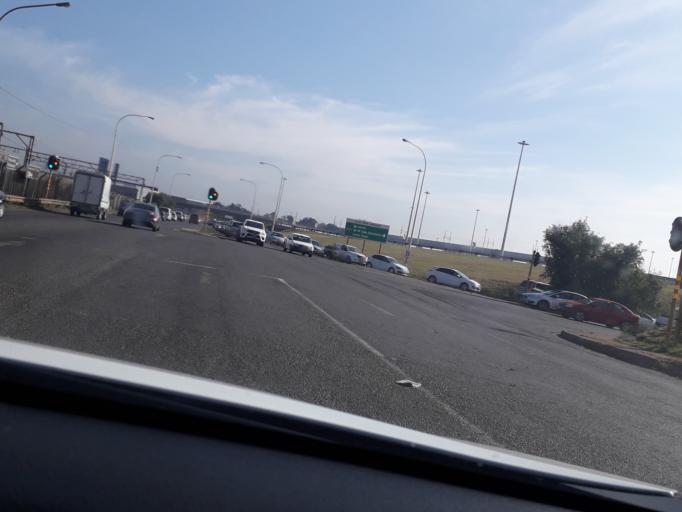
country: ZA
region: Gauteng
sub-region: City of Johannesburg Metropolitan Municipality
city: Modderfontein
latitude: -26.1339
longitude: 28.2228
